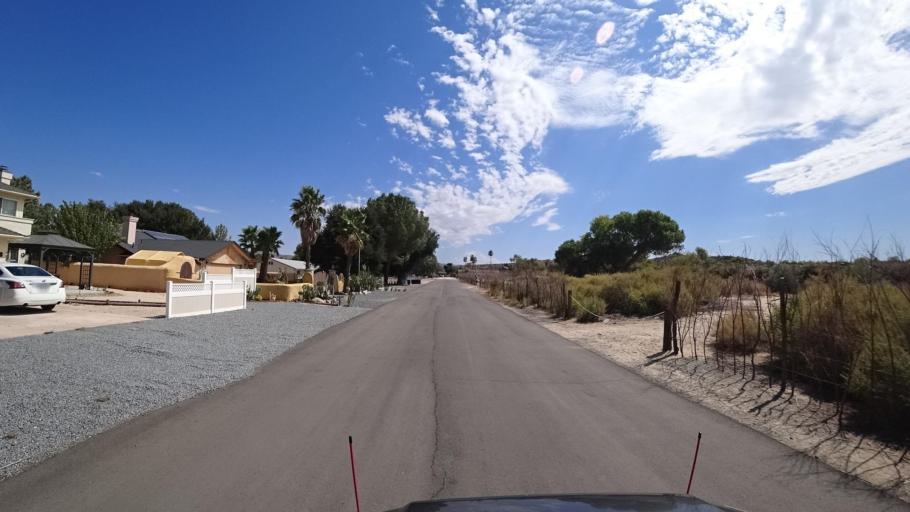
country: MX
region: Baja California
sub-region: Tecate
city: Cereso del Hongo
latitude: 32.6192
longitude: -116.1923
